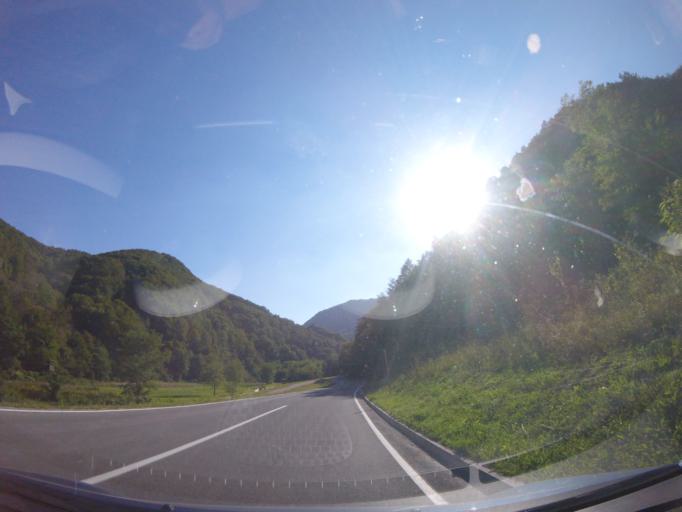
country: HR
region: Zagrebacka
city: Rude
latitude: 45.7849
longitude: 15.6907
